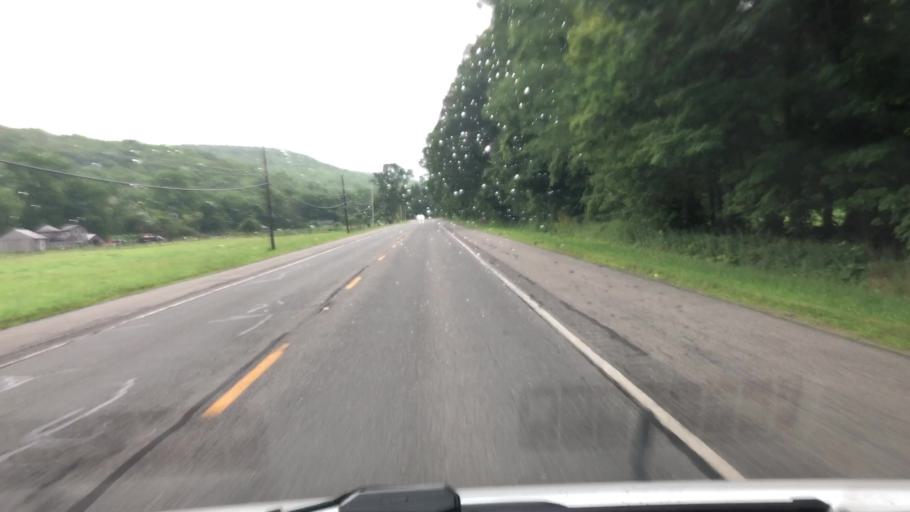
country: US
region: Massachusetts
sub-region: Berkshire County
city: Williamstown
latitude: 42.6348
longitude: -73.2262
